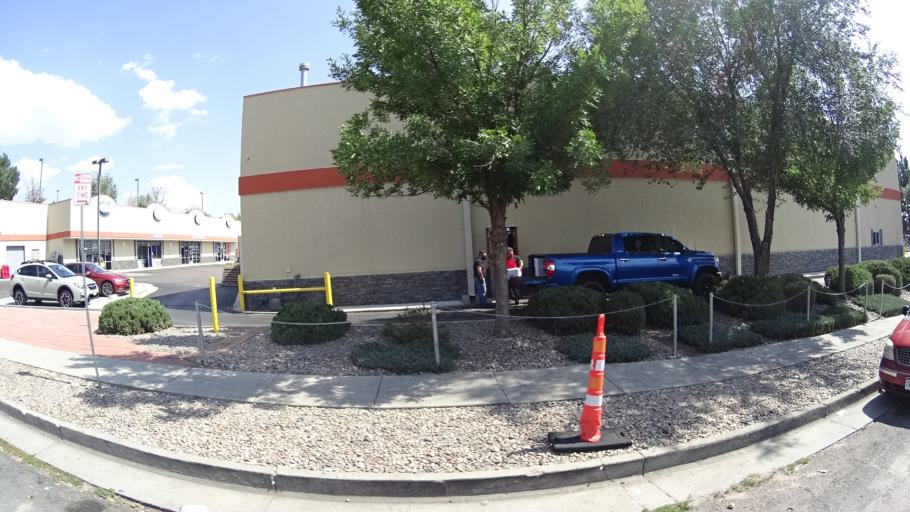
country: US
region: Colorado
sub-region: El Paso County
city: Colorado Springs
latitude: 38.8324
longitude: -104.7609
